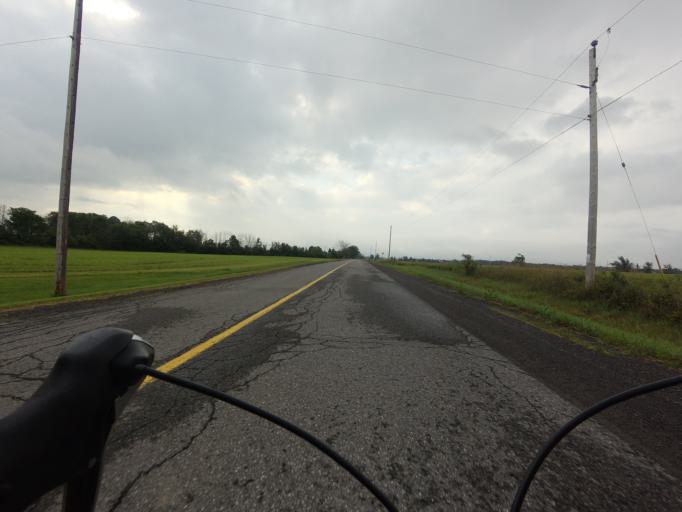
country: CA
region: Ontario
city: Bells Corners
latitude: 45.1217
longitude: -75.7753
